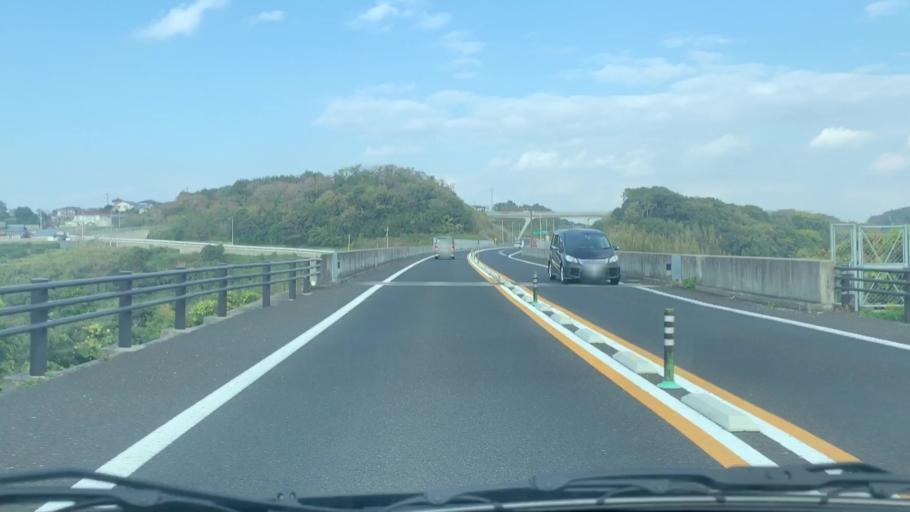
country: JP
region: Nagasaki
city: Sasebo
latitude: 33.0401
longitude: 129.7456
